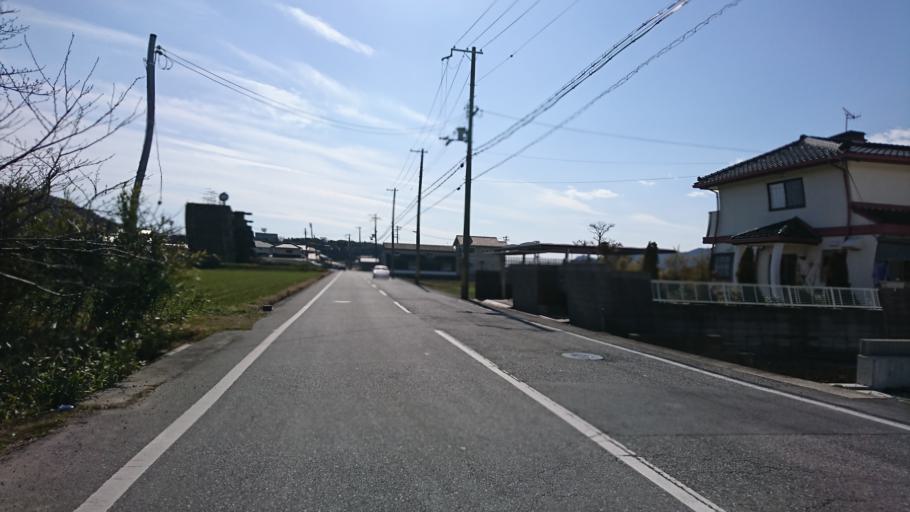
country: JP
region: Hyogo
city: Kakogawacho-honmachi
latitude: 34.8147
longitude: 134.8286
